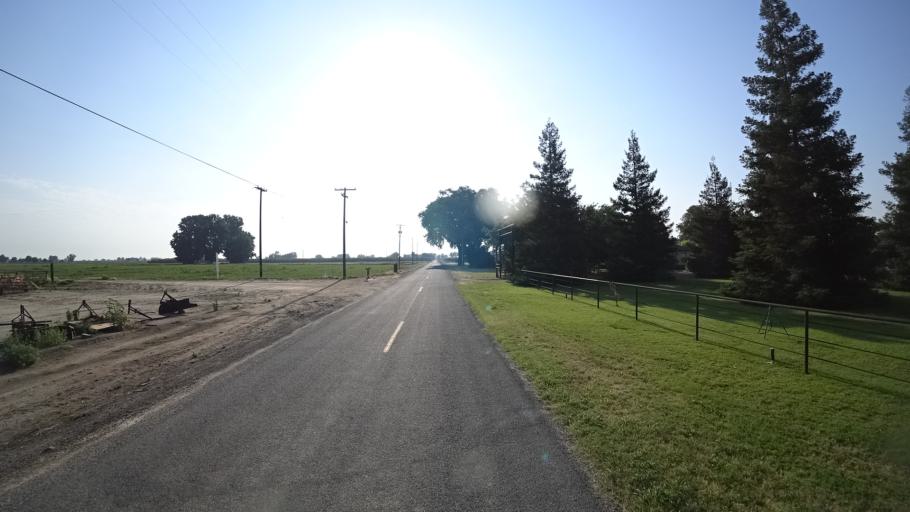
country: US
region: California
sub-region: Kings County
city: Lemoore
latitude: 36.3730
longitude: -119.8032
